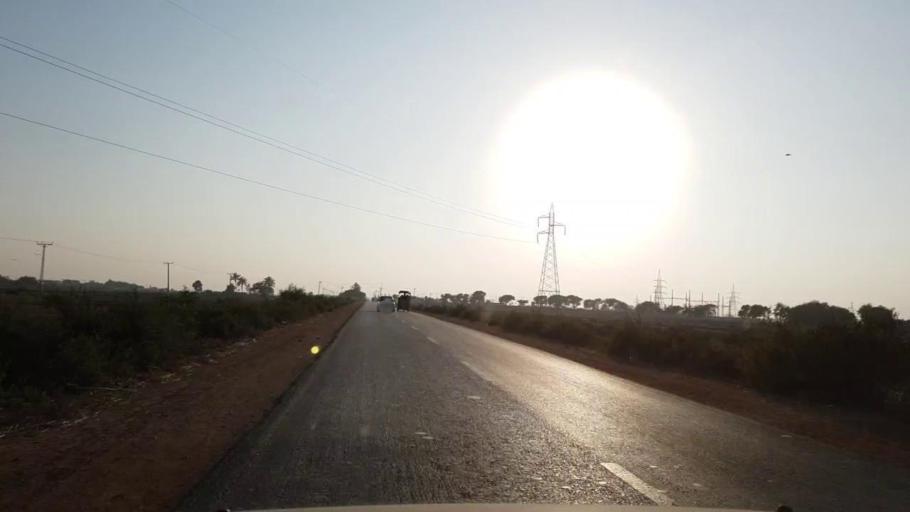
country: PK
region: Sindh
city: Daro Mehar
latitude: 24.6297
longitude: 68.1034
